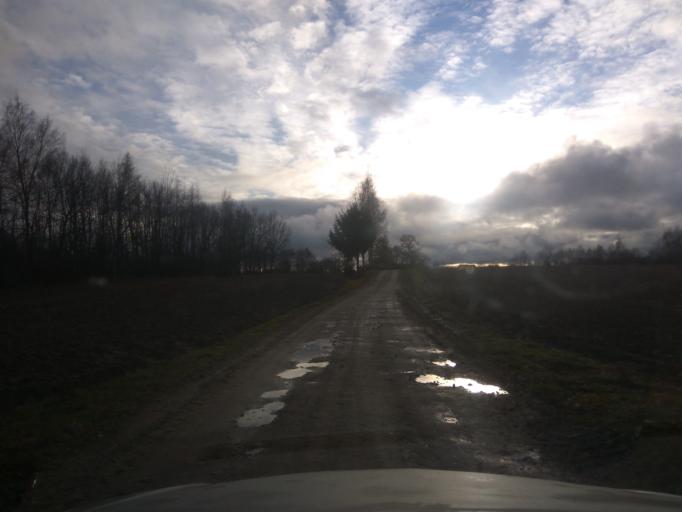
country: LV
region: Kuldigas Rajons
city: Kuldiga
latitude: 56.8342
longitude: 21.8277
